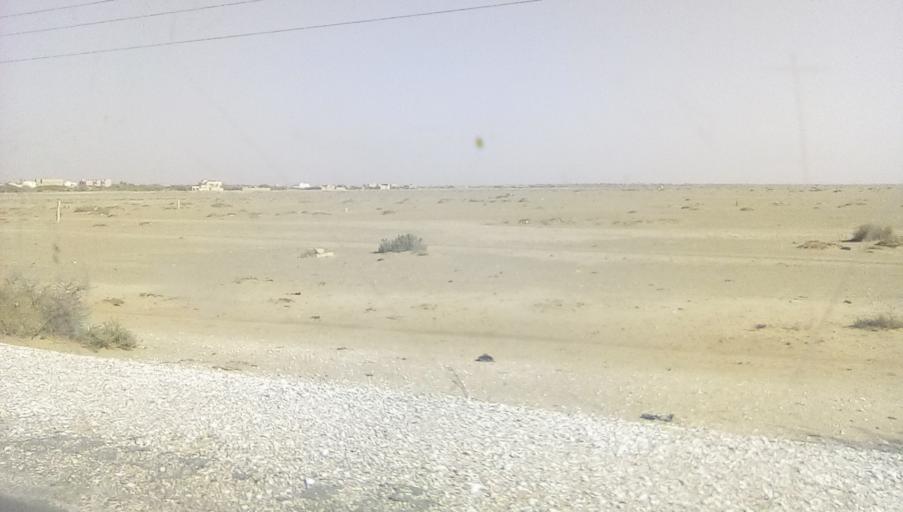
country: SN
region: Saint-Louis
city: Saint-Louis
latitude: 16.0389
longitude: -16.4542
